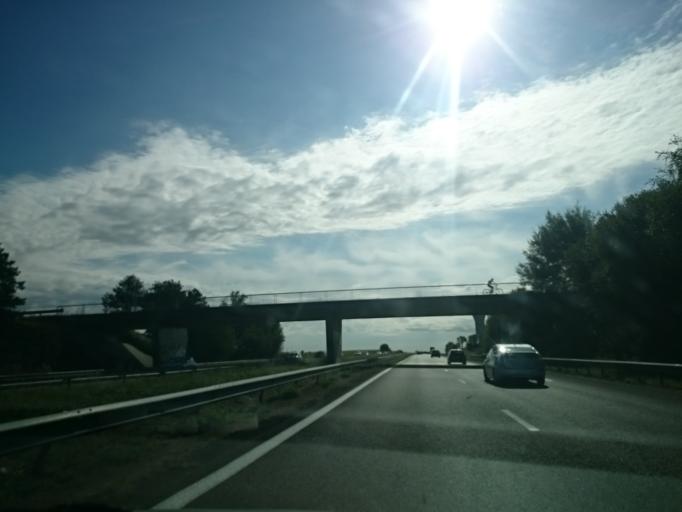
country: FR
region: Brittany
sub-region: Departement d'Ille-et-Vilaine
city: Bedee
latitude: 48.1848
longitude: -1.9450
